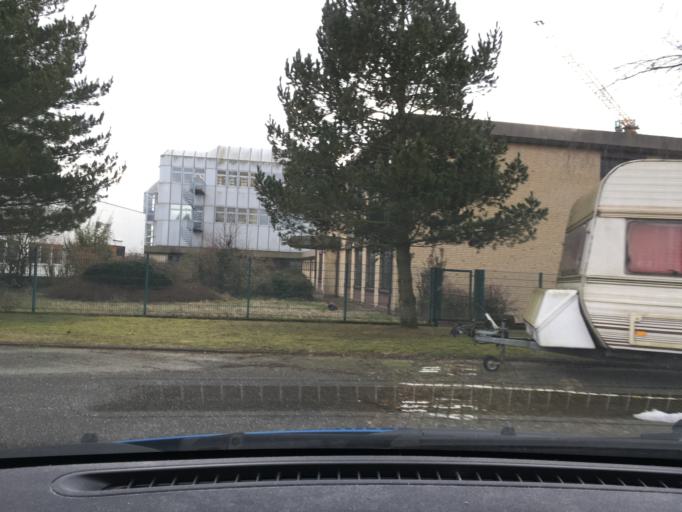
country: DE
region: Schleswig-Holstein
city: Wedel
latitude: 53.5792
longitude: 9.7278
